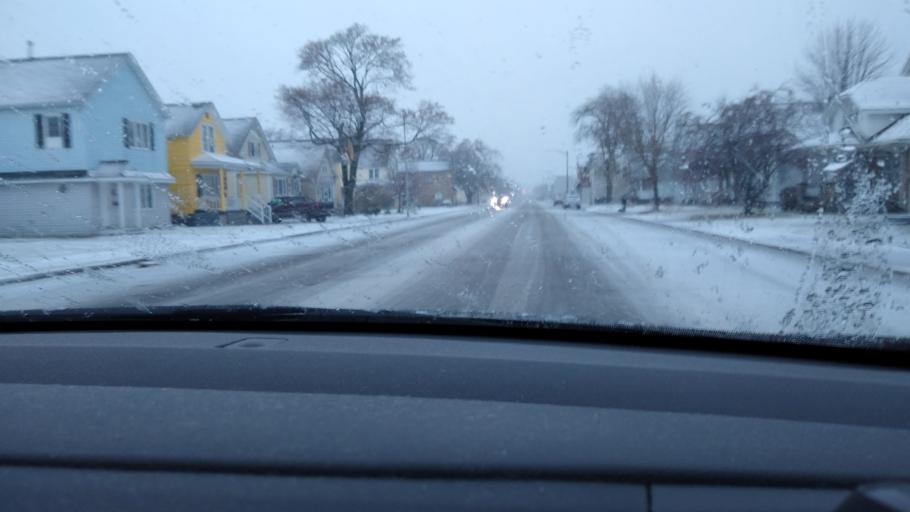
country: US
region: Michigan
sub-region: Delta County
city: Escanaba
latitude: 45.7410
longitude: -87.0612
